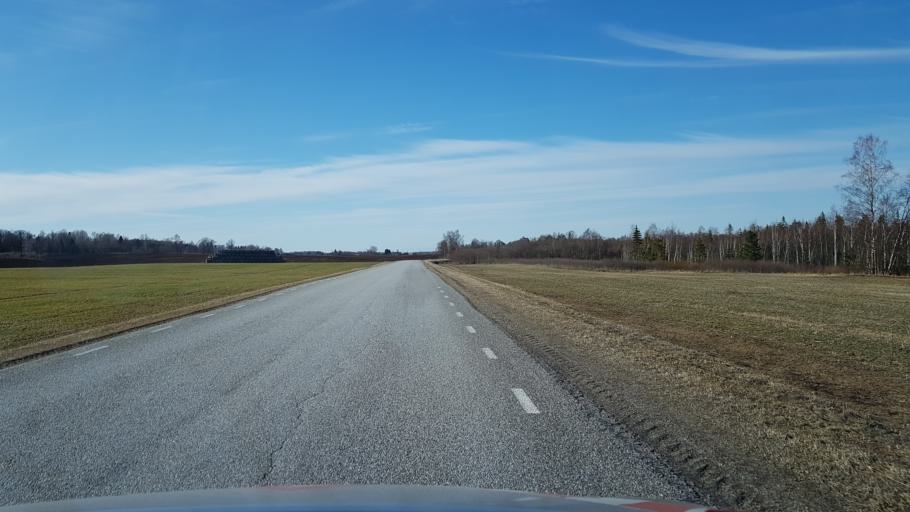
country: EE
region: Laeaene-Virumaa
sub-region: Kadrina vald
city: Kadrina
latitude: 59.3002
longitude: 26.1626
